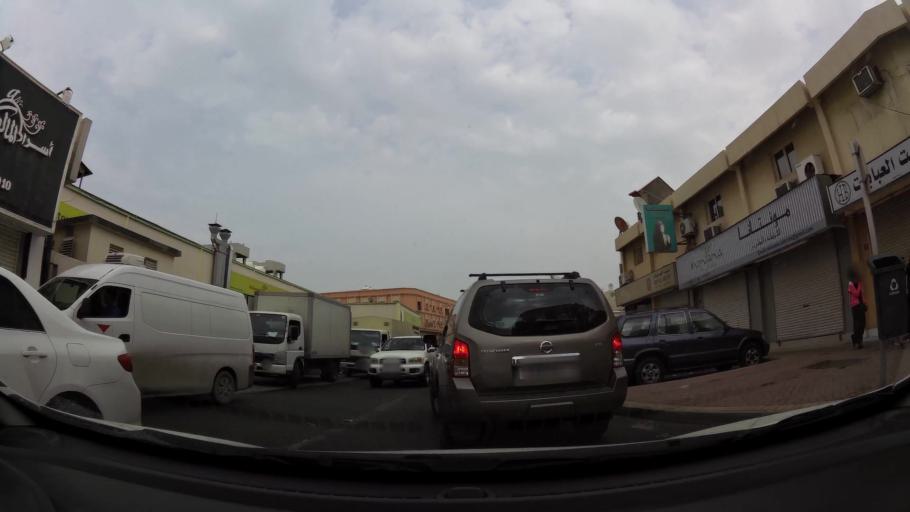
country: BH
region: Northern
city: Ar Rifa'
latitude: 26.1329
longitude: 50.5526
